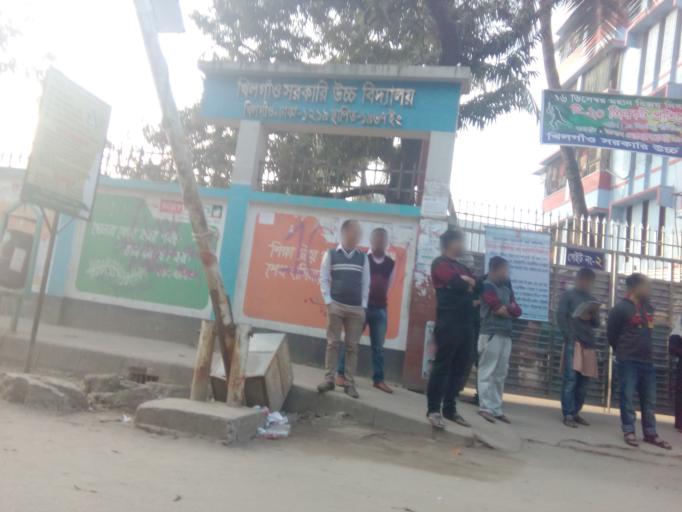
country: BD
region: Dhaka
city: Paltan
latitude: 23.7509
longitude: 90.4209
